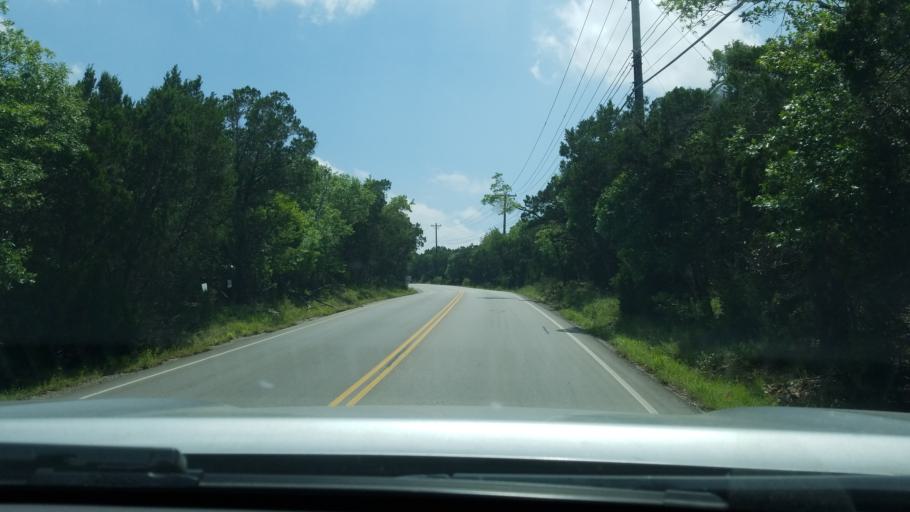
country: US
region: Texas
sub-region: Hays County
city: Woodcreek
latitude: 30.0250
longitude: -98.1303
